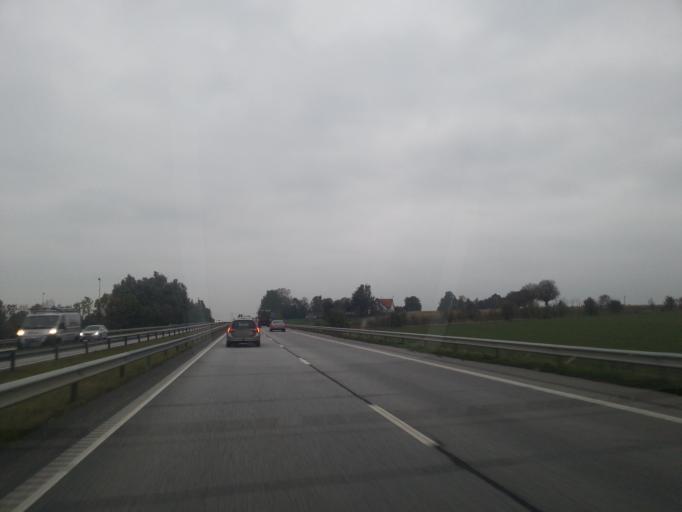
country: SE
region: Skane
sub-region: Malmo
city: Tygelsjo
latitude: 55.5139
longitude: 13.0132
